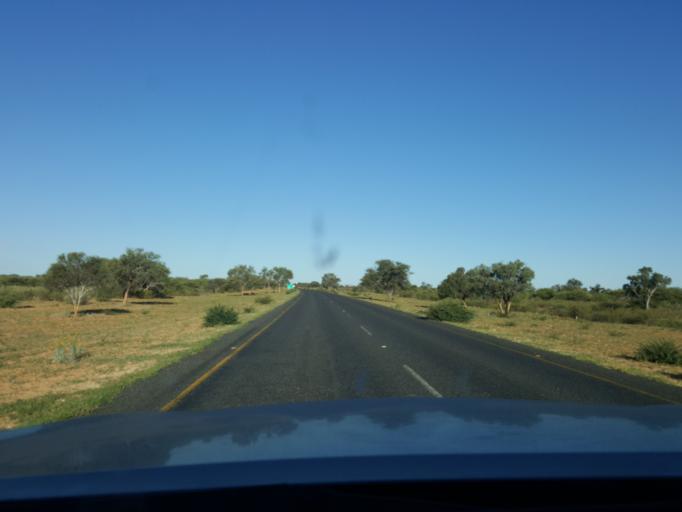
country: BW
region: Southern
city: Khakhea
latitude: -24.2319
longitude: 23.2499
